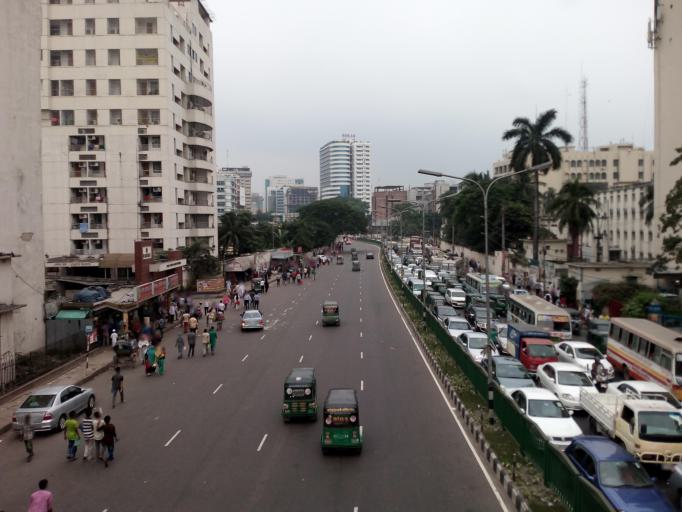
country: BD
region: Dhaka
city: Azimpur
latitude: 23.7390
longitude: 90.3960
